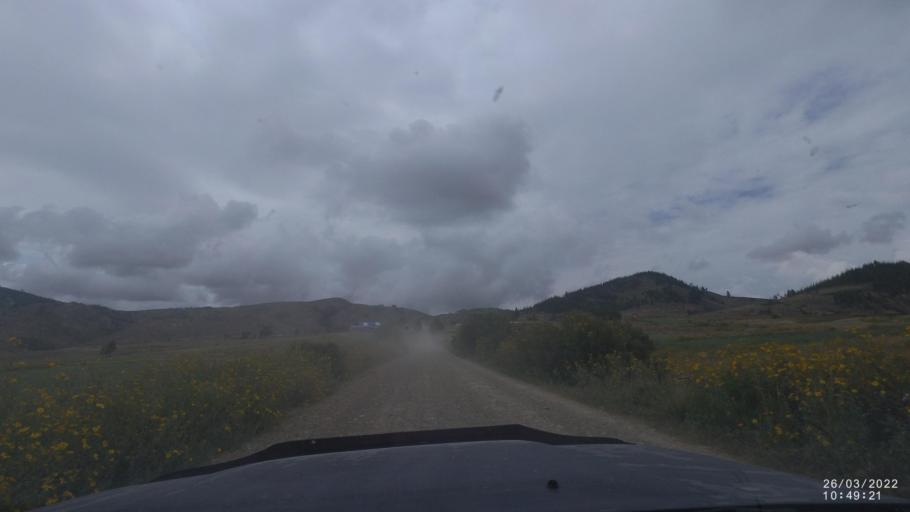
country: BO
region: Cochabamba
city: Tarata
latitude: -17.5021
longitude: -66.0386
